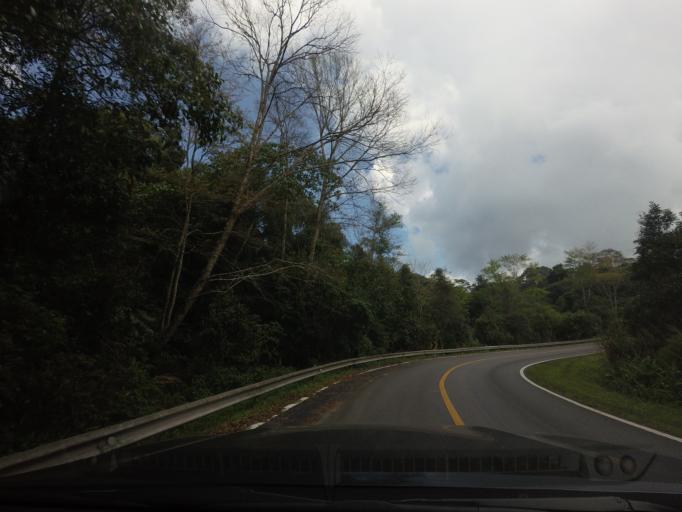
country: TH
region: Phetchabun
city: Lom Kao
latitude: 16.9589
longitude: 101.0230
